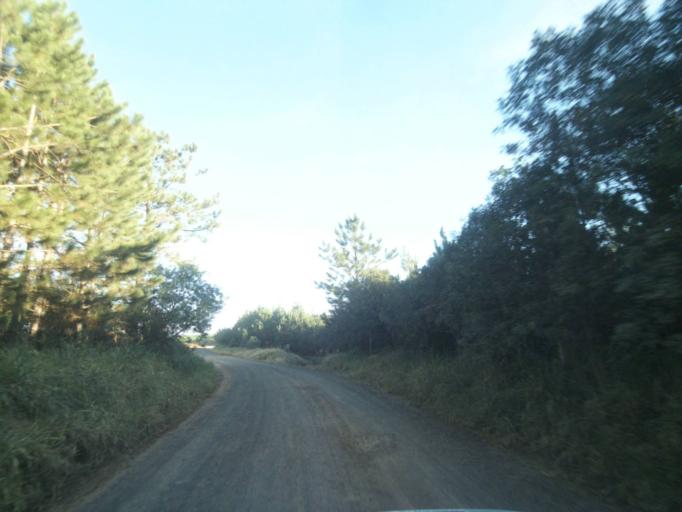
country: BR
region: Parana
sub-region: Telemaco Borba
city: Telemaco Borba
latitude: -24.4287
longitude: -50.5971
